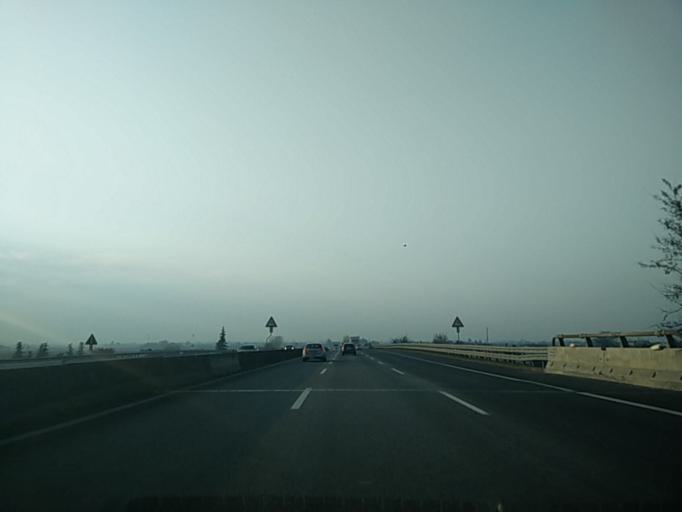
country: IT
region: Emilia-Romagna
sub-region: Provincia di Ravenna
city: Solarolo
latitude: 44.3460
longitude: 11.8399
